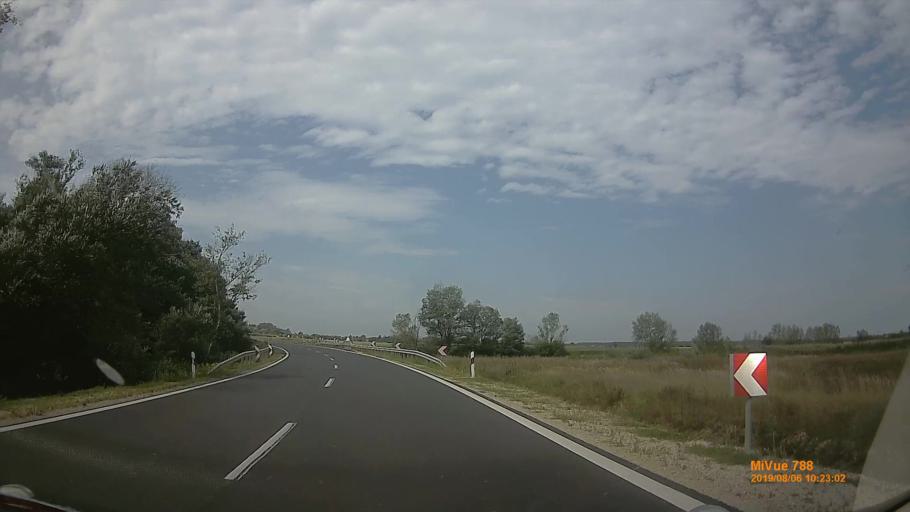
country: HU
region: Vas
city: Vasvar
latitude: 47.0645
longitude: 16.7214
